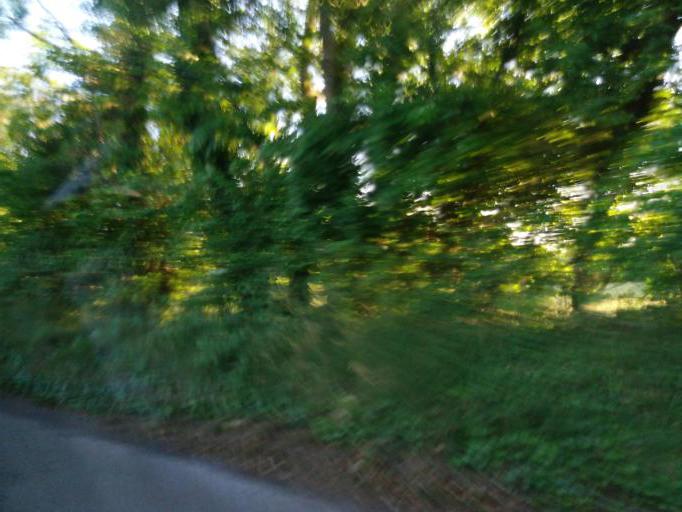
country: IE
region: Leinster
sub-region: An Mhi
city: Ashbourne
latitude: 53.5508
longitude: -6.3609
